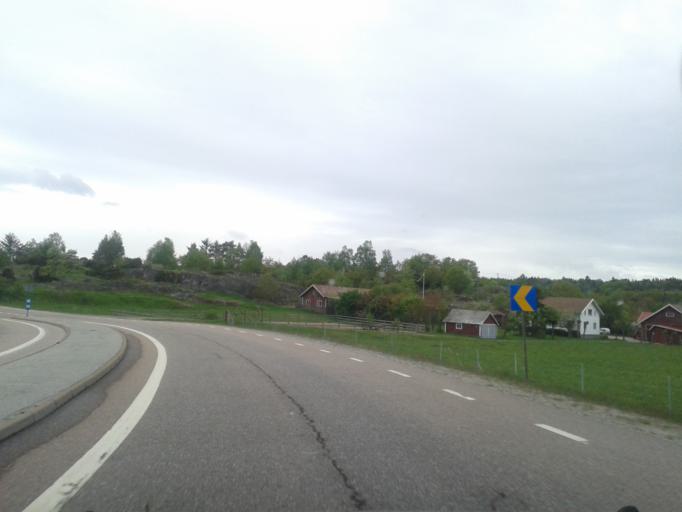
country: SE
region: Vaestra Goetaland
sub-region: Stenungsunds Kommun
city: Stora Hoga
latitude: 58.0263
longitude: 11.8421
